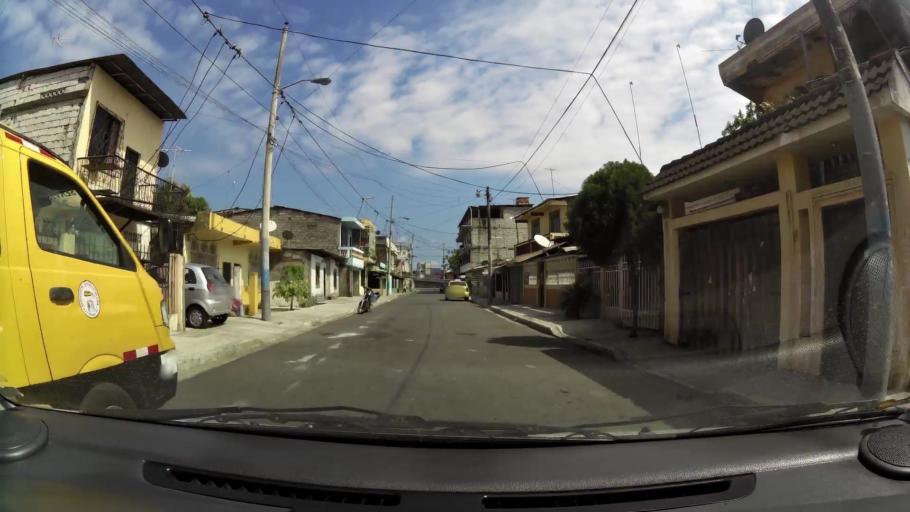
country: EC
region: Guayas
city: Guayaquil
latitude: -2.2572
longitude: -79.8928
